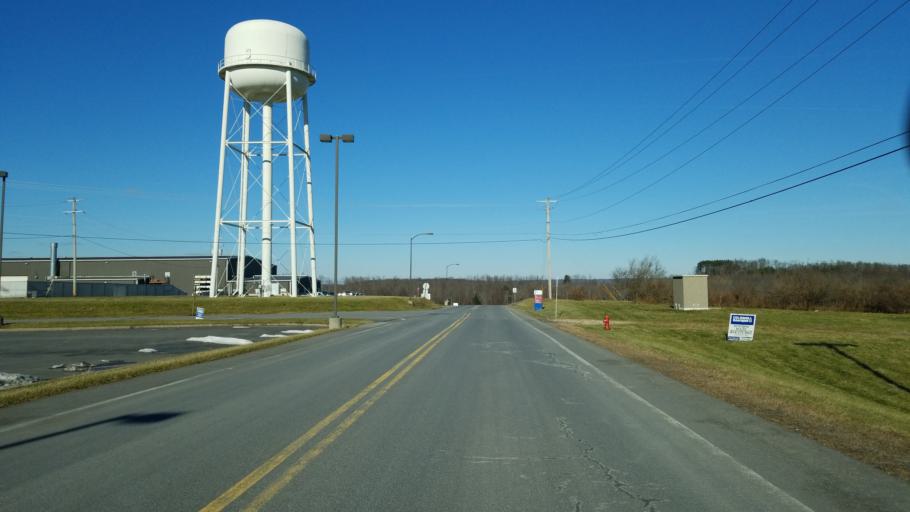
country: US
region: Pennsylvania
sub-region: Jefferson County
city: Reynoldsville
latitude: 41.1843
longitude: -78.8918
